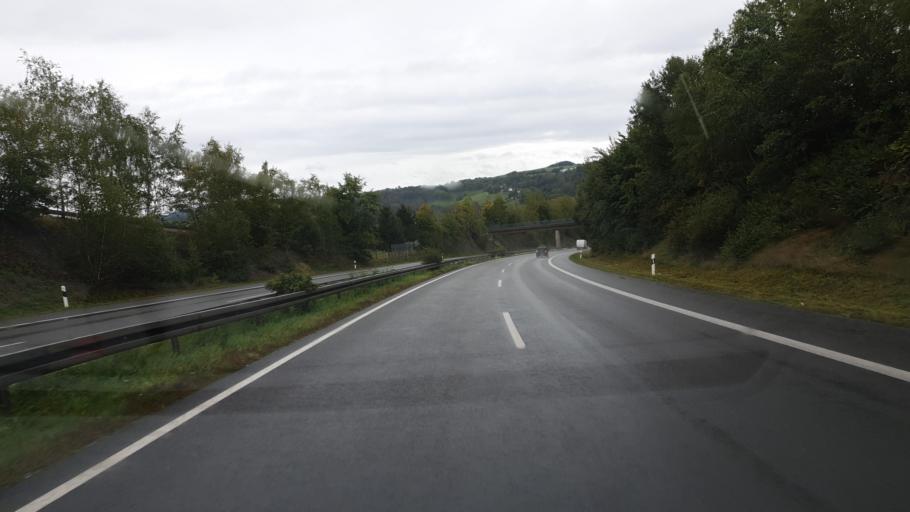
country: DE
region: Saxony
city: Zschopau
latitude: 50.7474
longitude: 13.0558
